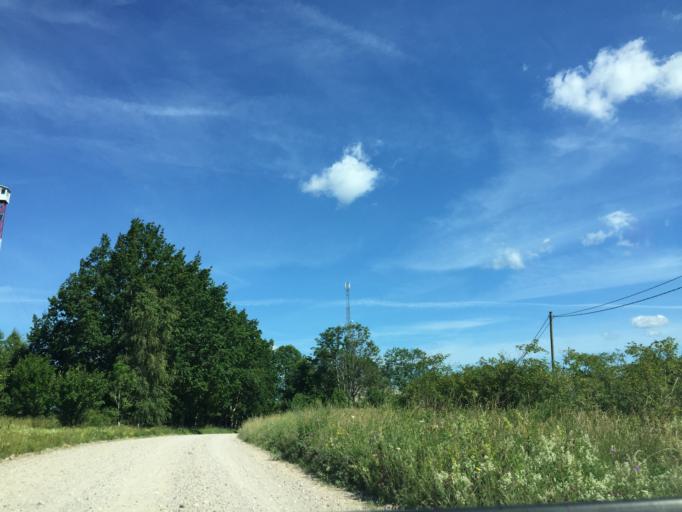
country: LV
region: Dundaga
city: Dundaga
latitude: 57.3579
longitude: 22.0313
